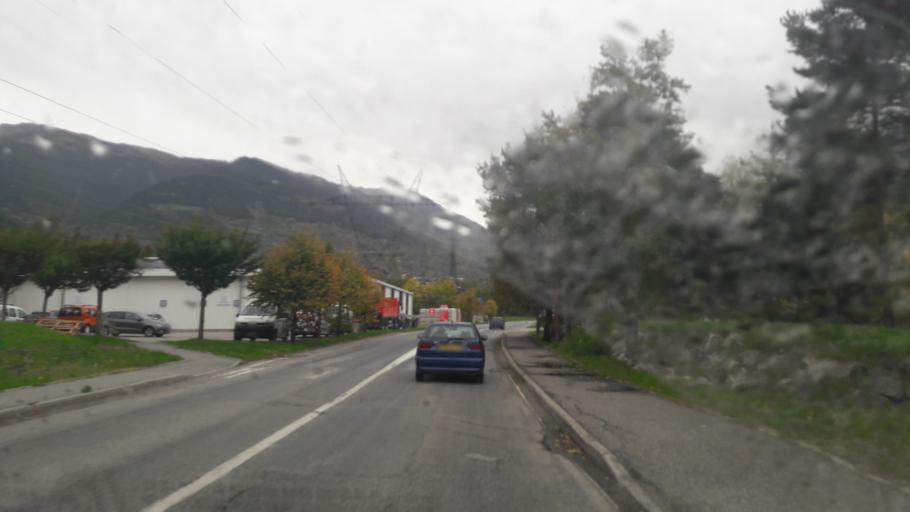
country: FR
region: Rhone-Alpes
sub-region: Departement de la Savoie
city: Bourg-Saint-Maurice
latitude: 45.6231
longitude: 6.7825
